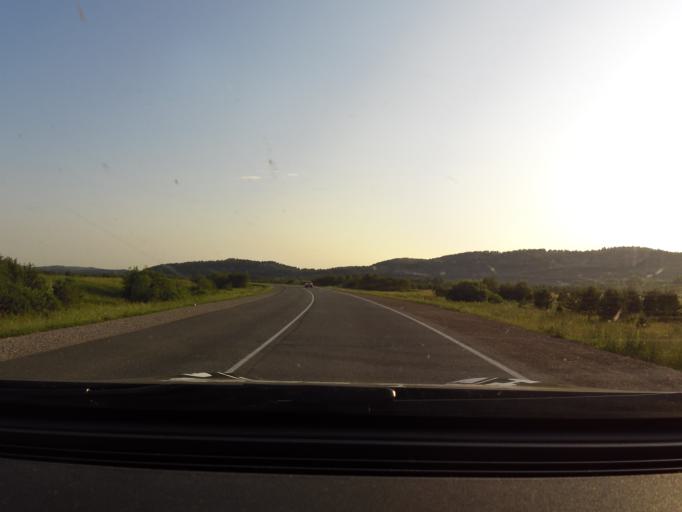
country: RU
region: Sverdlovsk
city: Mikhaylovsk
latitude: 56.4558
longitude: 59.0918
